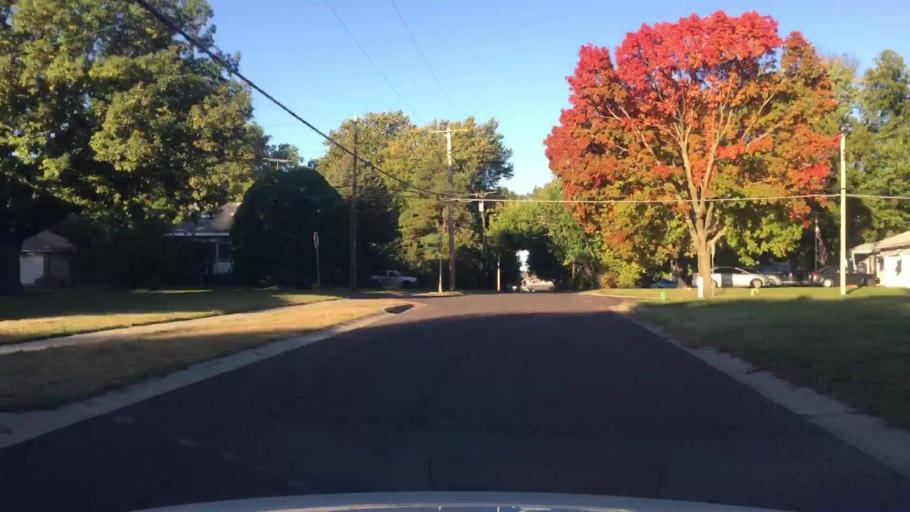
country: US
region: Kansas
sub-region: Johnson County
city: Overland Park
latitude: 39.0041
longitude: -94.6684
